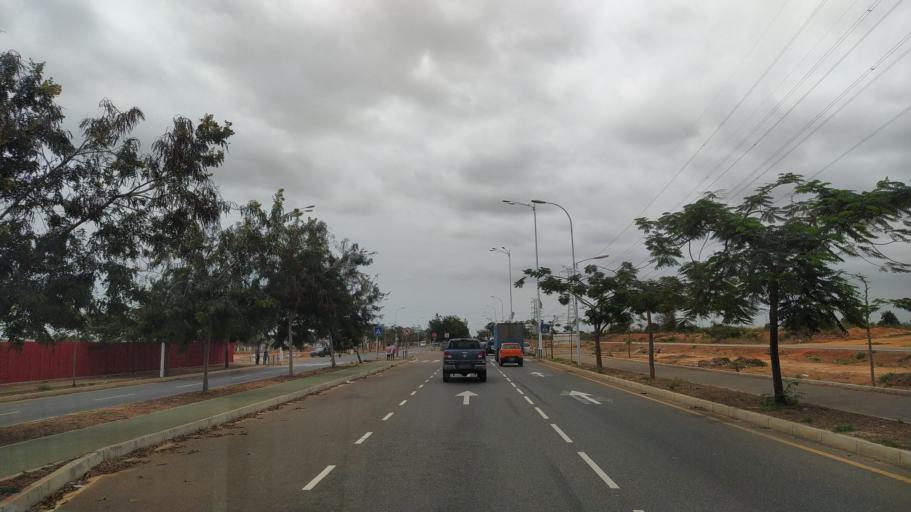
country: AO
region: Luanda
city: Luanda
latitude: -8.9849
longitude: 13.2521
